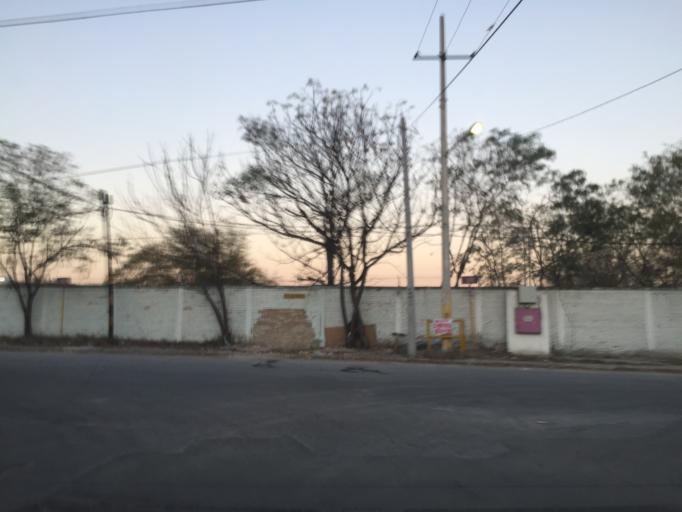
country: MX
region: Nuevo Leon
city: Guadalupe
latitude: 25.6994
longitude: -100.2228
